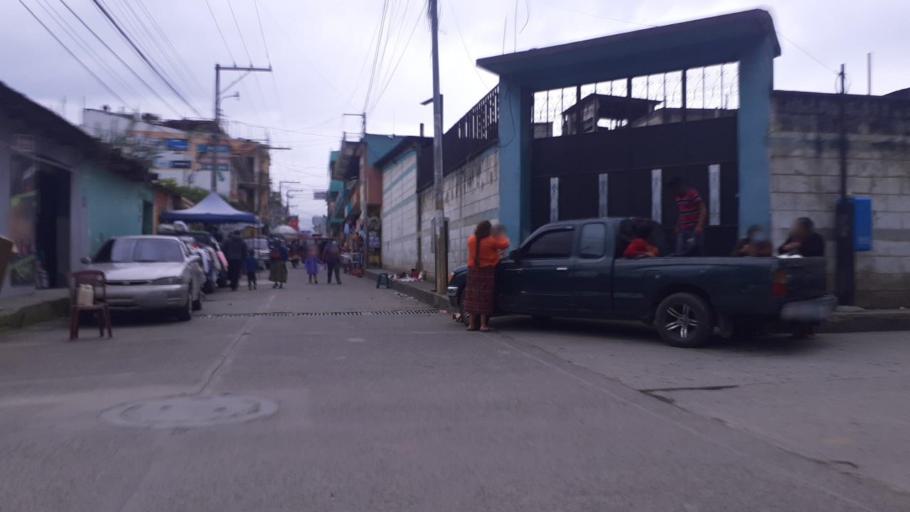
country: GT
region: Quetzaltenango
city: Ostuncalco
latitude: 14.8707
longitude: -91.6215
